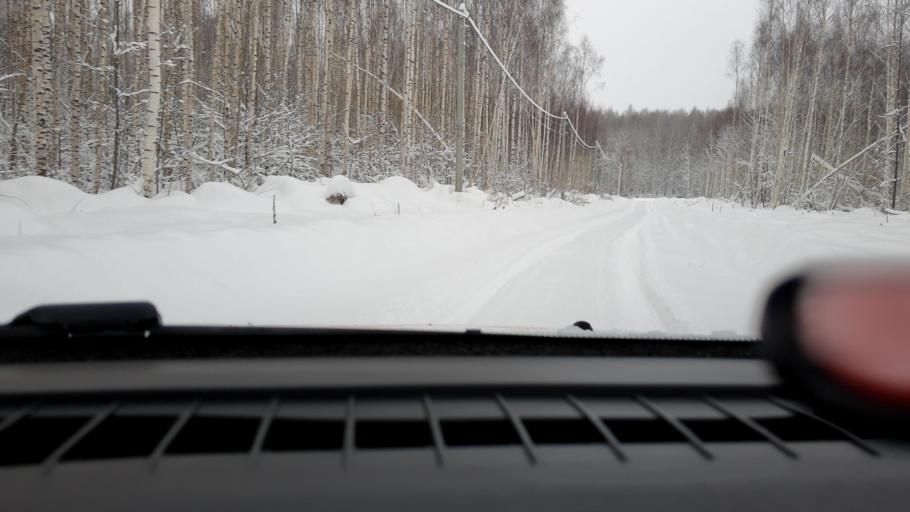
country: RU
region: Nizjnij Novgorod
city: Afonino
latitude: 56.1308
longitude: 43.9725
